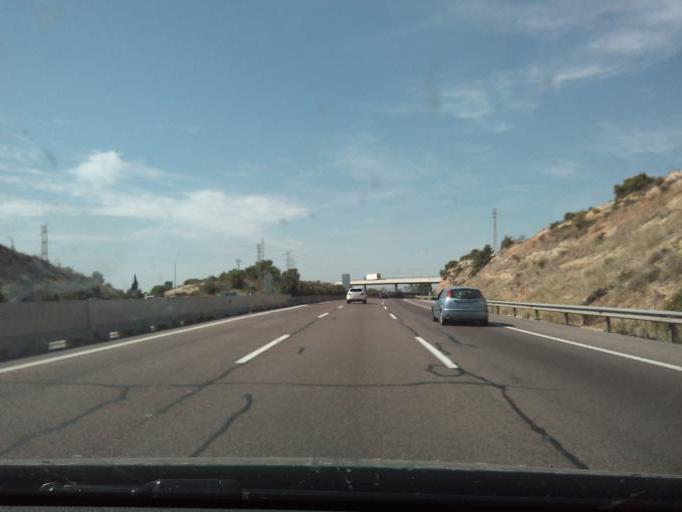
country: ES
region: Valencia
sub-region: Provincia de Valencia
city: Manises
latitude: 39.5193
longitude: -0.4775
